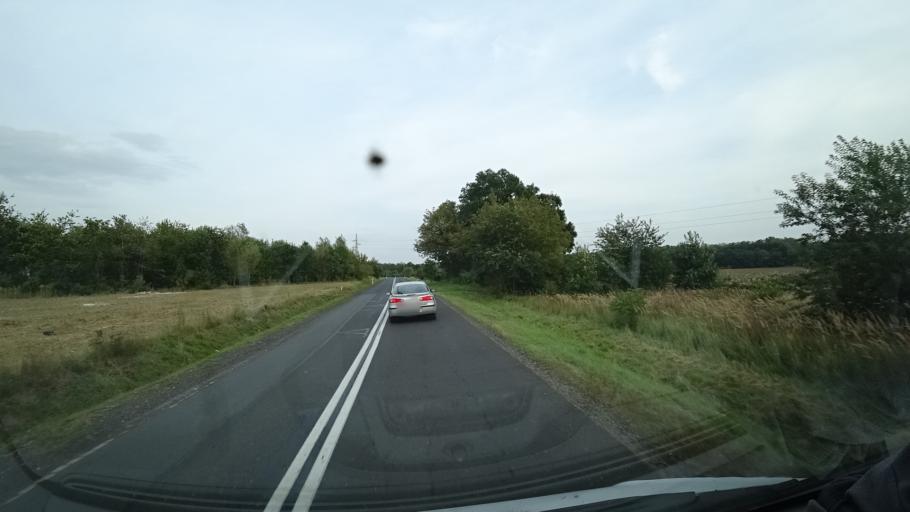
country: PL
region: Silesian Voivodeship
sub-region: Powiat gliwicki
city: Toszek
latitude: 50.3856
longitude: 18.5436
